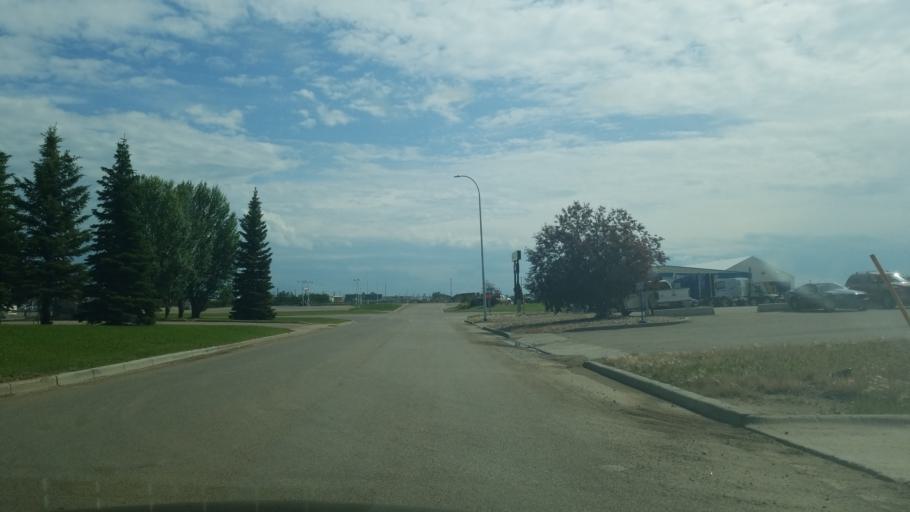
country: CA
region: Saskatchewan
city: Lloydminster
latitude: 53.2875
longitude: -110.0368
